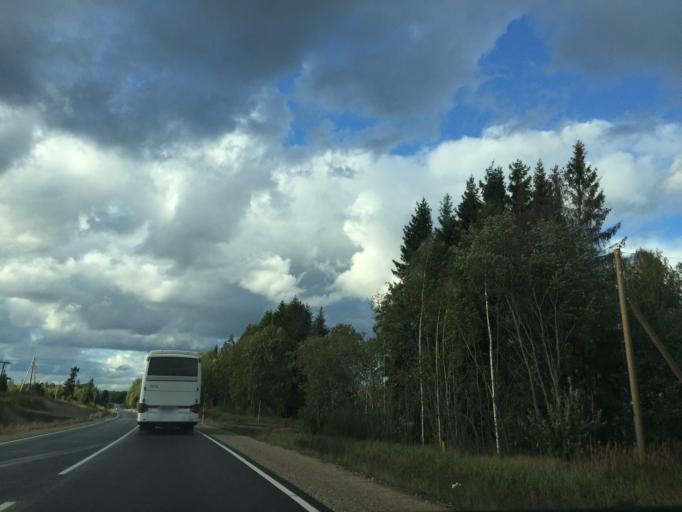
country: LV
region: Ligatne
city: Ligatne
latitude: 57.1435
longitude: 25.0790
